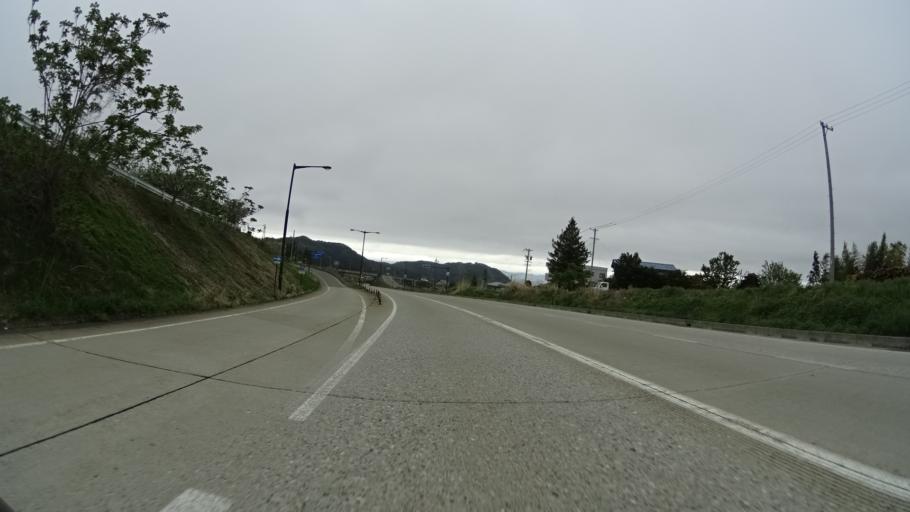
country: JP
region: Nagano
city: Nakano
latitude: 36.7344
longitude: 138.4181
